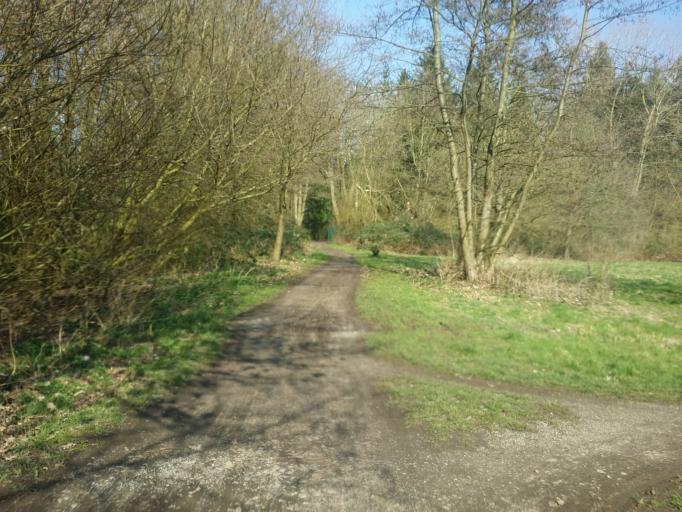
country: DE
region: Lower Saxony
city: Stuhr
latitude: 53.0402
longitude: 8.7451
